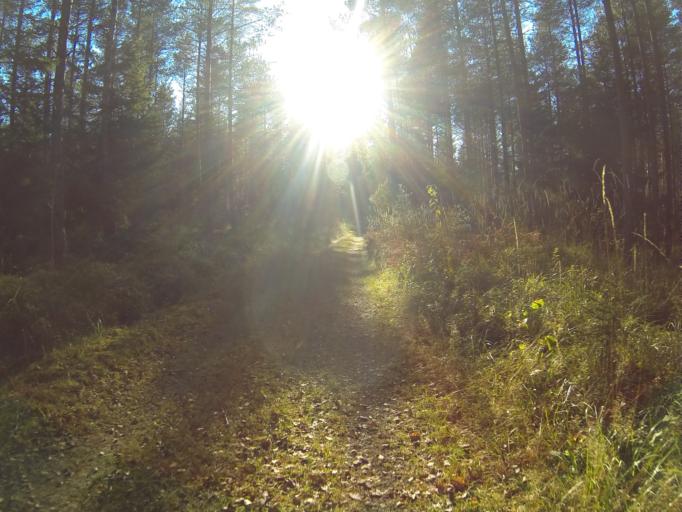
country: FI
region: Varsinais-Suomi
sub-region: Salo
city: Saerkisalo
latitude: 60.2248
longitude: 22.9691
